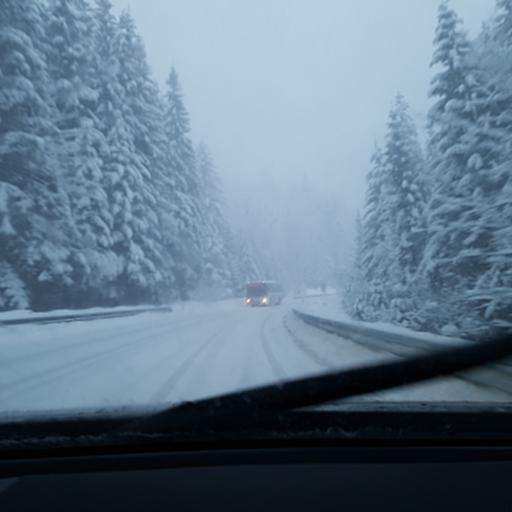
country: AT
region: Upper Austria
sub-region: Politischer Bezirk Gmunden
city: Bad Goisern
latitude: 47.5889
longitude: 13.5107
